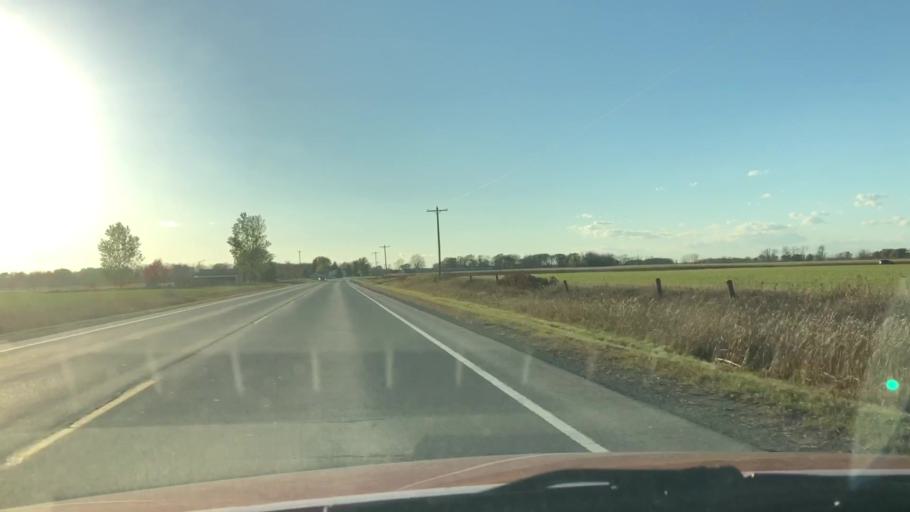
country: US
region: Wisconsin
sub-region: Brown County
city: Oneida
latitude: 44.4446
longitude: -88.1464
